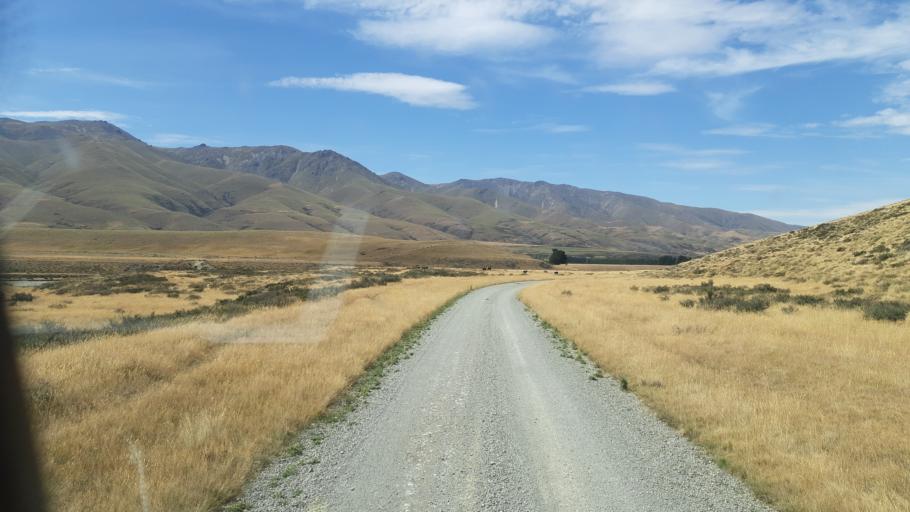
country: NZ
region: Canterbury
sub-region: Timaru District
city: Pleasant Point
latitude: -44.3518
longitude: 170.6300
